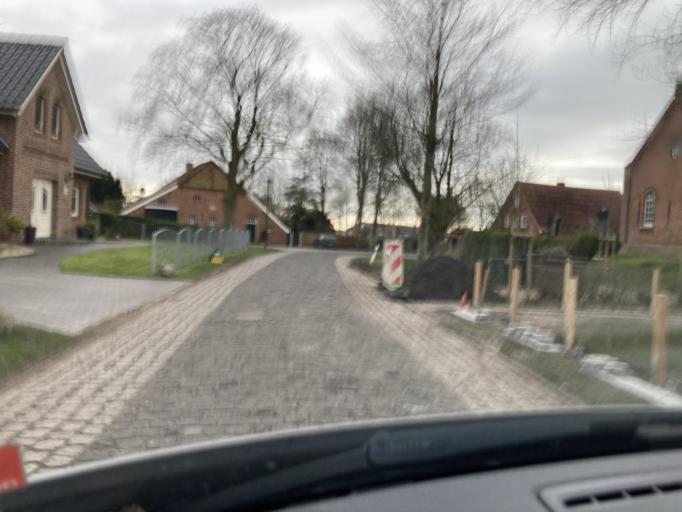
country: DE
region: Lower Saxony
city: Leer
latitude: 53.1948
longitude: 7.4193
